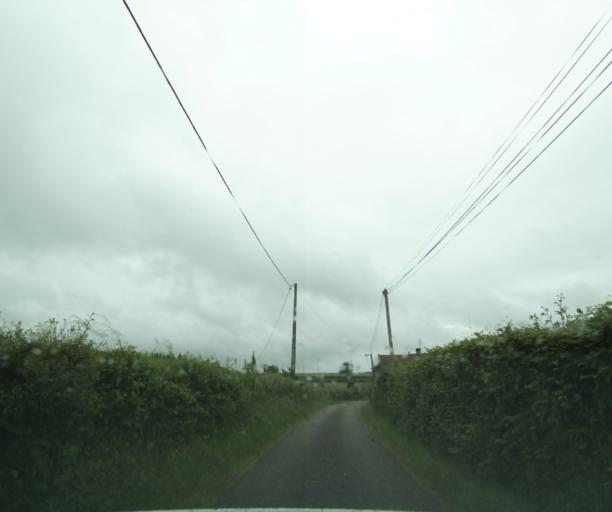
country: FR
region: Bourgogne
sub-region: Departement de Saone-et-Loire
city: Matour
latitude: 46.4843
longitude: 4.4648
